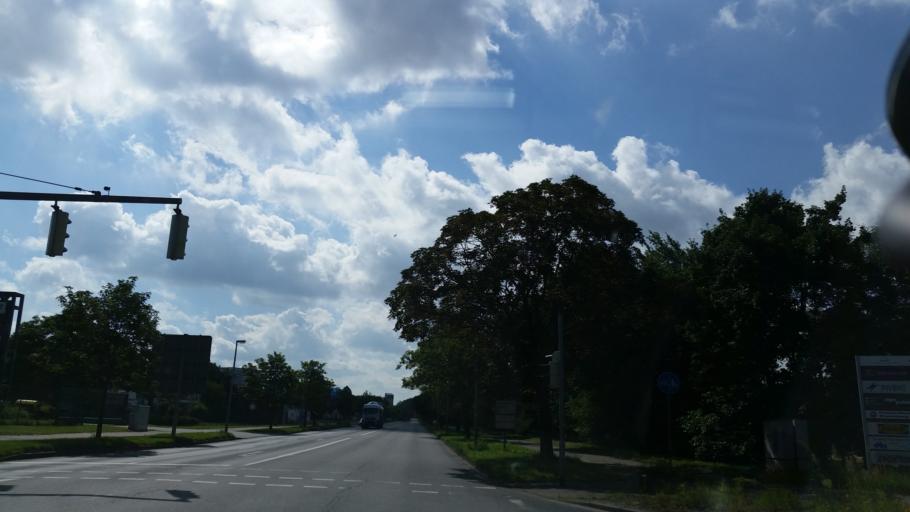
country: DE
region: Lower Saxony
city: Klein Schwulper
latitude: 52.3229
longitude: 10.4757
